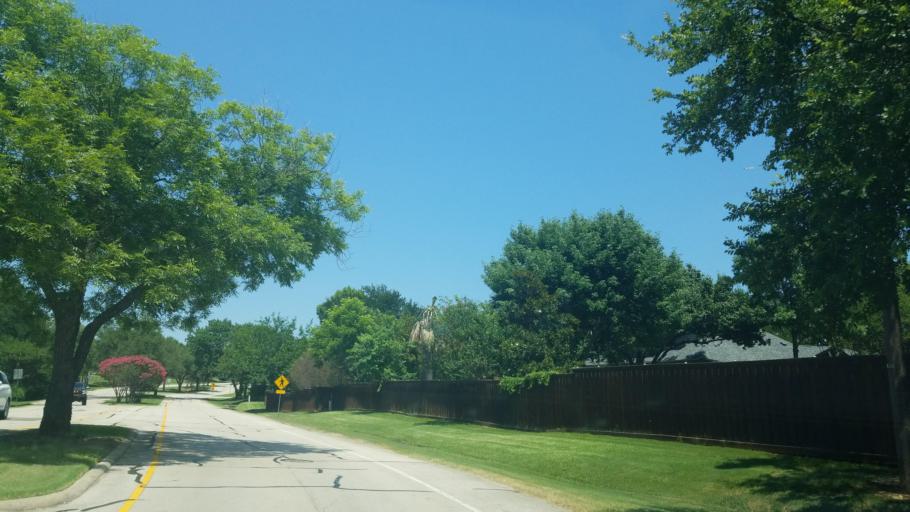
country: US
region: Texas
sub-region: Denton County
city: Highland Village
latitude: 33.0845
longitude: -97.0586
